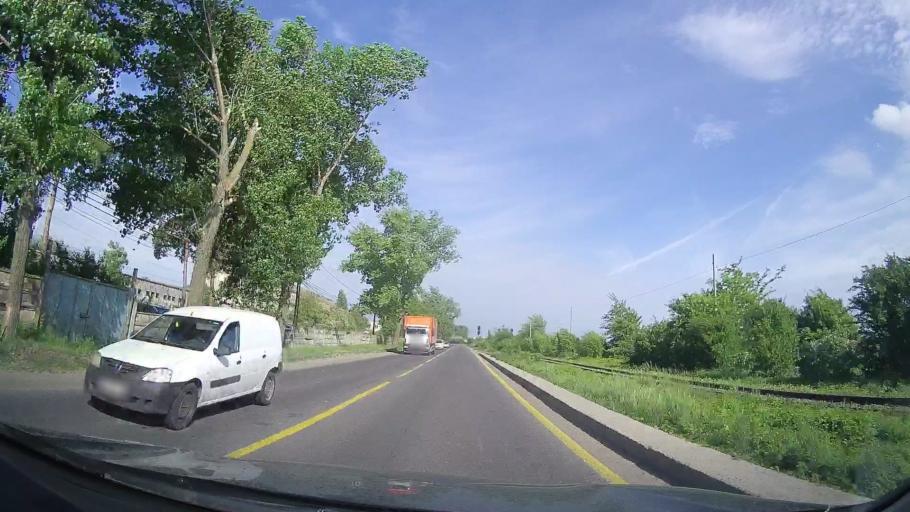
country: RO
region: Ilfov
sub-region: Comuna Magurele
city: Magurele
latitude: 44.3644
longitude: 26.0221
